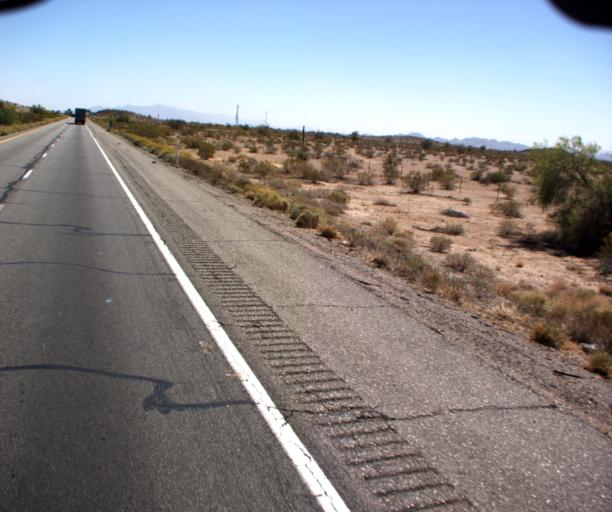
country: US
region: Arizona
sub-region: Maricopa County
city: Buckeye
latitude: 33.4334
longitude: -112.6534
